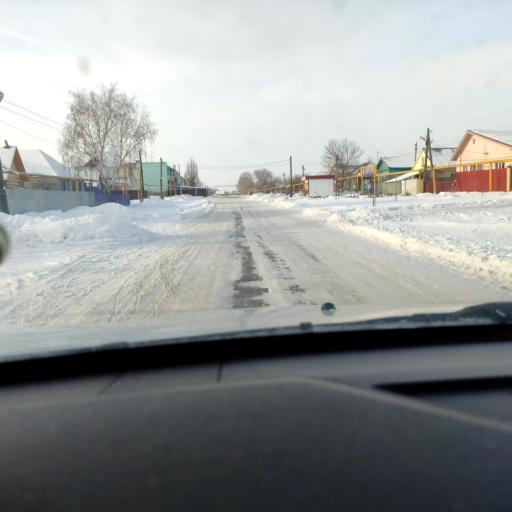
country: RU
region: Samara
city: Smyshlyayevka
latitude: 53.1652
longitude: 50.3872
